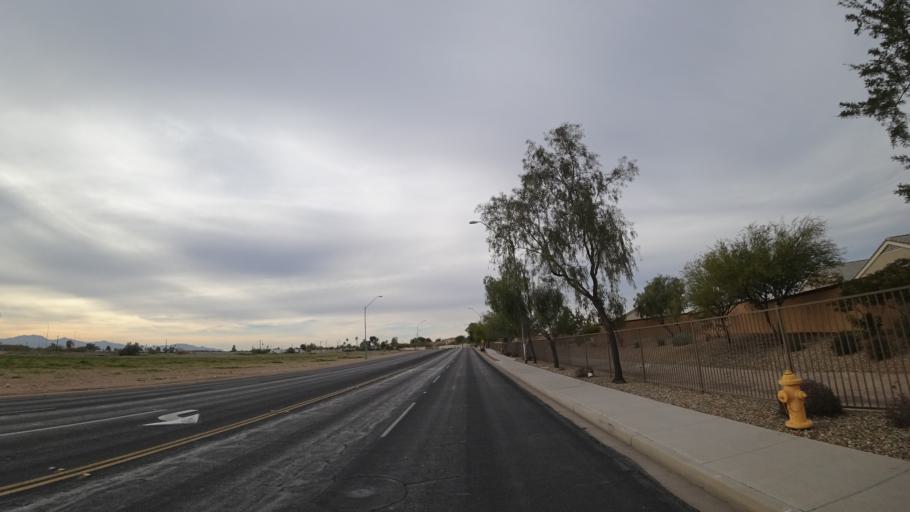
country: US
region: Arizona
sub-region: Maricopa County
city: El Mirage
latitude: 33.6220
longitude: -112.3211
